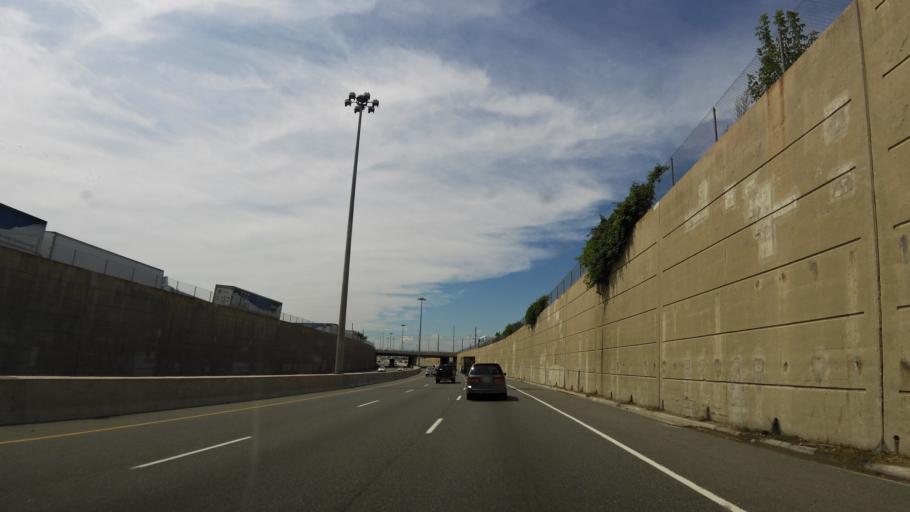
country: CA
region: Ontario
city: Etobicoke
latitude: 43.6986
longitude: -79.5834
